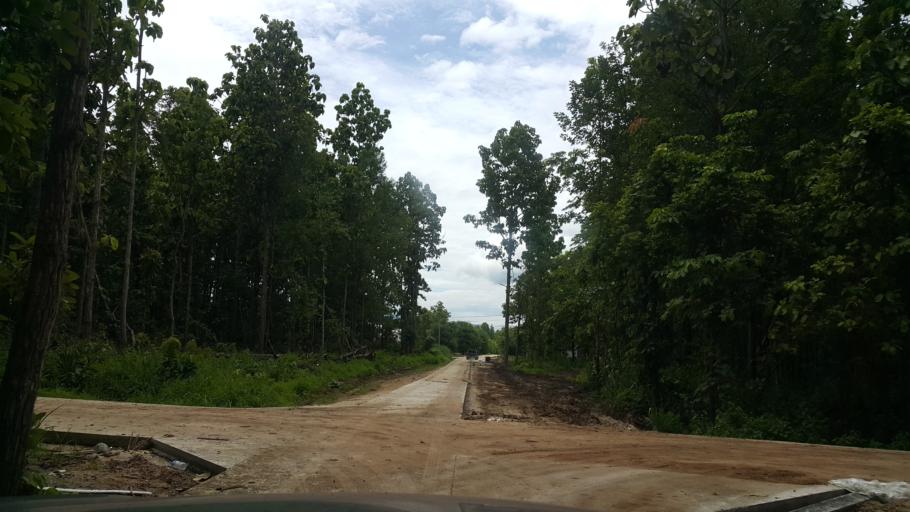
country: TH
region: Chiang Mai
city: Mae Taeng
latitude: 19.1701
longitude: 98.9535
